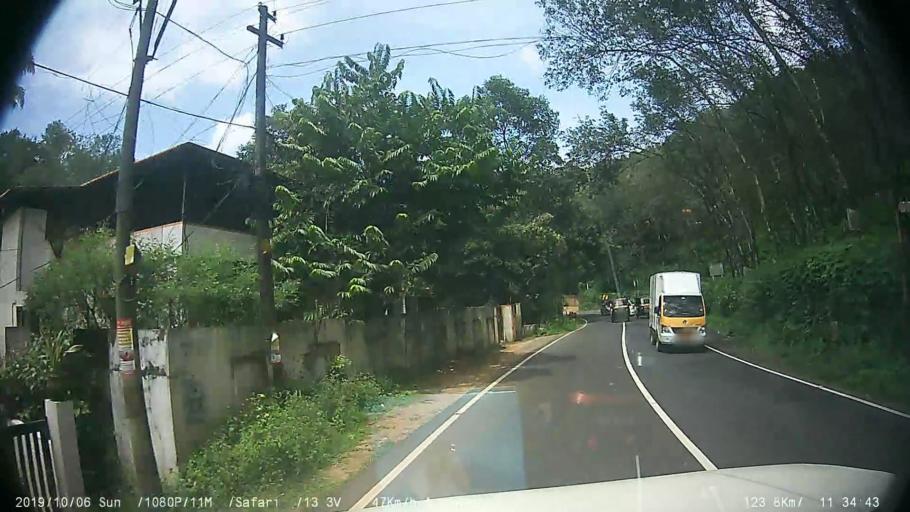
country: IN
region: Kerala
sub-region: Kottayam
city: Erattupetta
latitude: 9.5382
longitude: 76.8978
